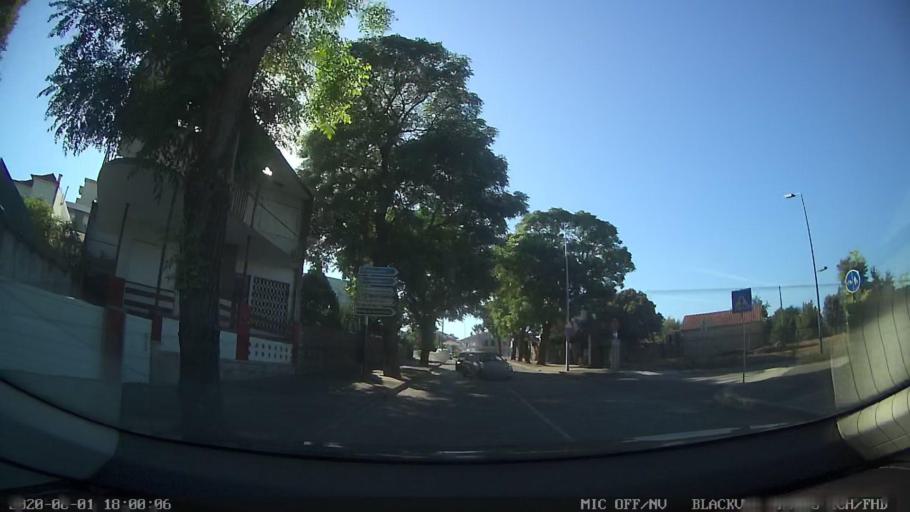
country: PT
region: Porto
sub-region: Santo Tirso
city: Santo Tirso
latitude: 41.3463
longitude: -8.4740
